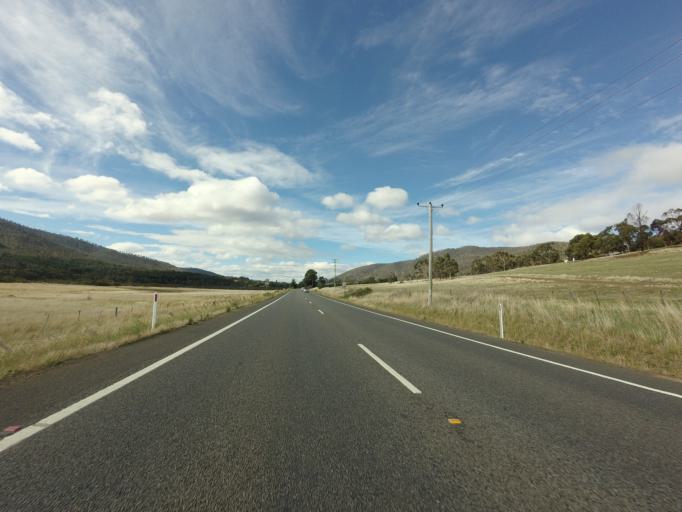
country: AU
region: Tasmania
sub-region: Derwent Valley
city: New Norfolk
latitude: -42.7757
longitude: 147.1175
